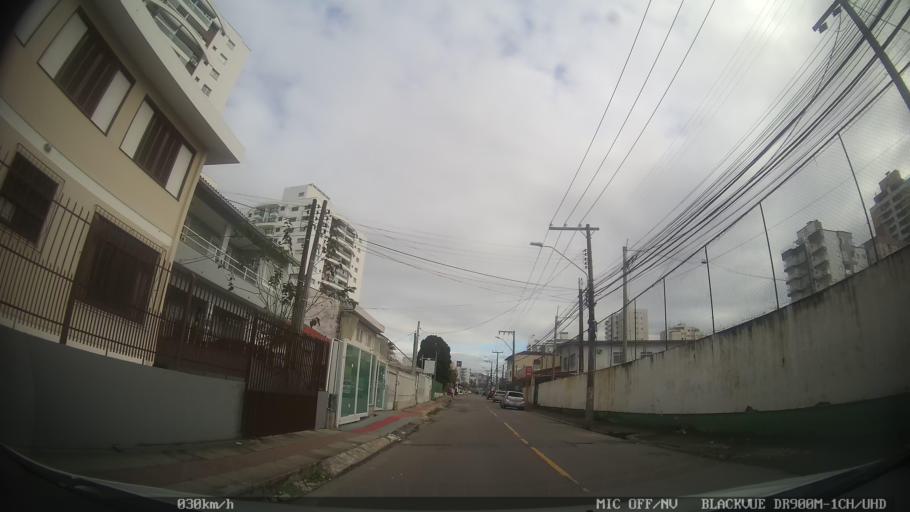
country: BR
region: Santa Catarina
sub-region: Sao Jose
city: Campinas
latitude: -27.5708
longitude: -48.6082
